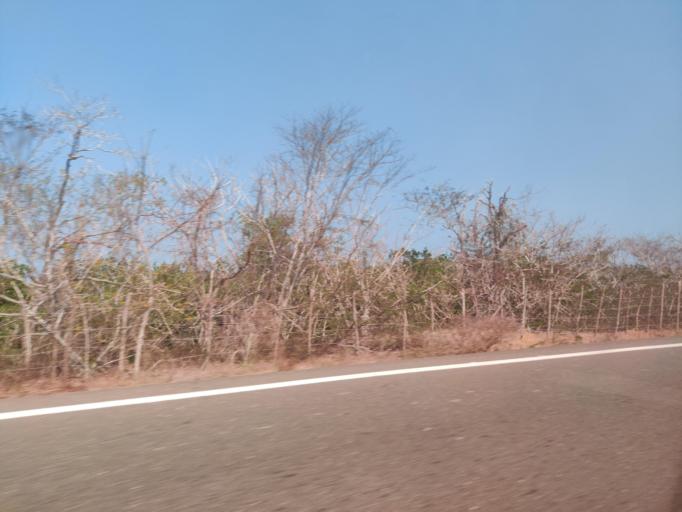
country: CO
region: Bolivar
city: Turbana
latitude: 10.1683
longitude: -75.6498
